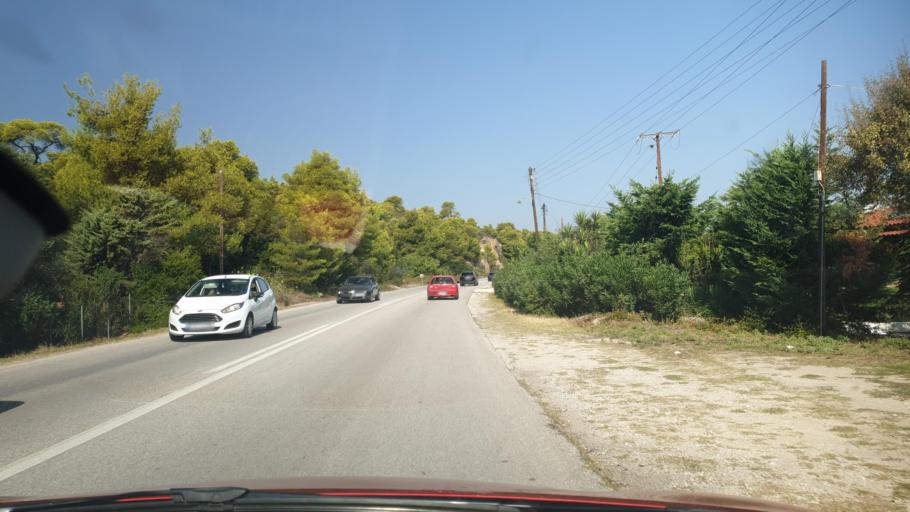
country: GR
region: Central Macedonia
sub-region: Nomos Chalkidikis
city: Agios Nikolaos
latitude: 40.2287
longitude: 23.7381
